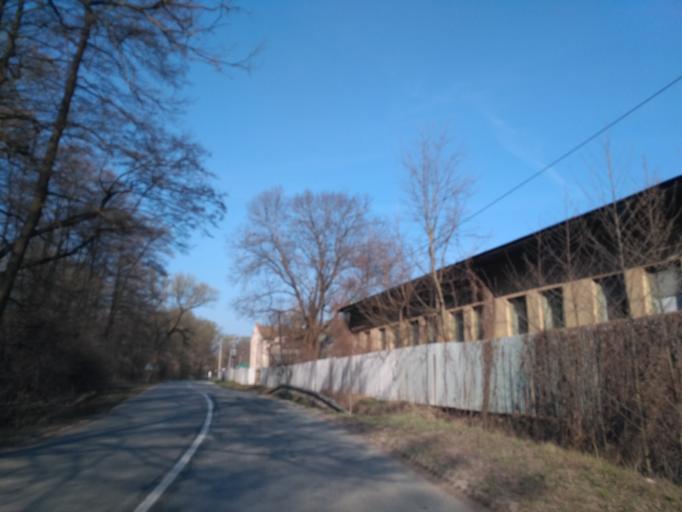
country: SK
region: Kosicky
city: Medzev
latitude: 48.6940
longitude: 20.9453
